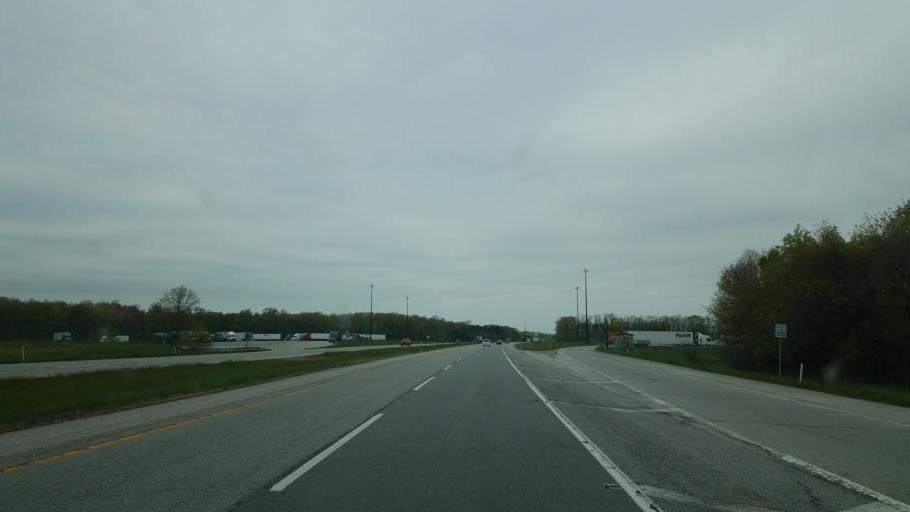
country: US
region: Michigan
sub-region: Saint Joseph County
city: White Pigeon
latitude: 41.7497
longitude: -85.6625
